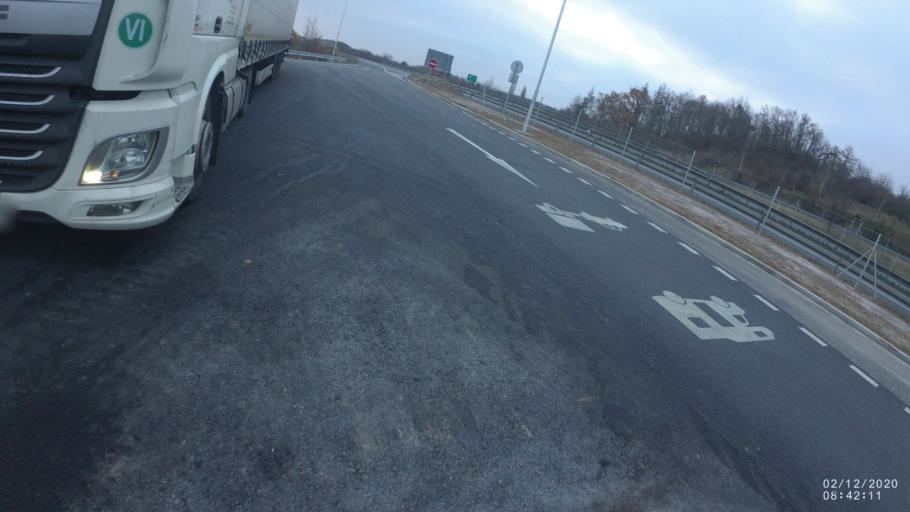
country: CZ
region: Plzensky
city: Dobrany
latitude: 49.6782
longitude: 13.3316
